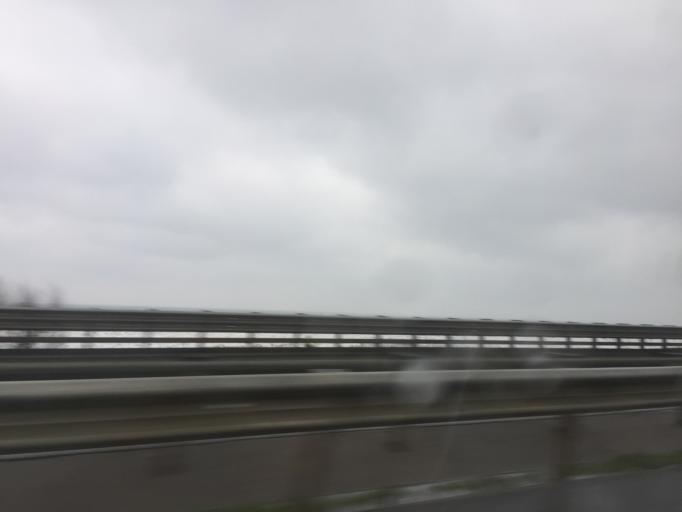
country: TR
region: Zonguldak
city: Alapli
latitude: 41.1112
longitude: 31.2786
